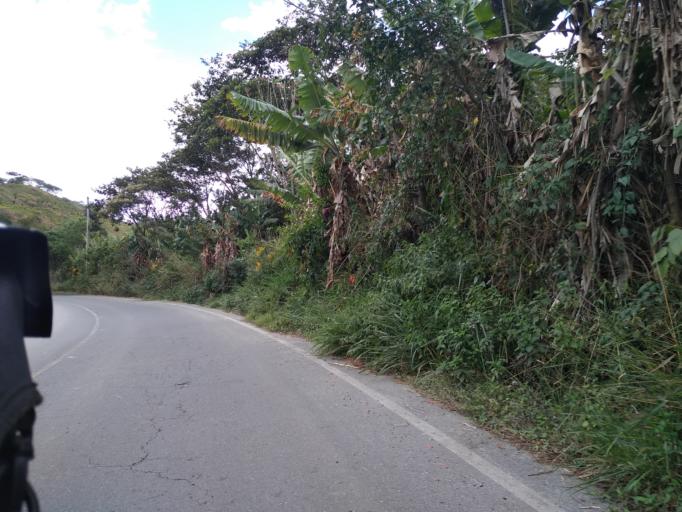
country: EC
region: Loja
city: Loja
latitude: -4.2116
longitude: -79.2328
